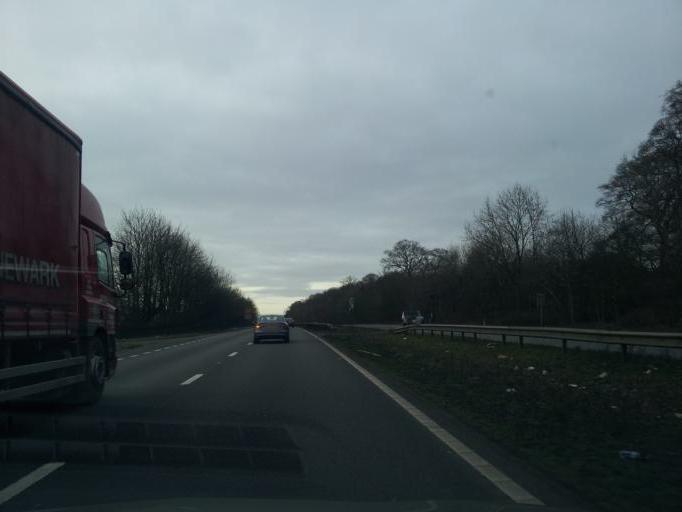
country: GB
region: England
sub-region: Lincolnshire
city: Grantham
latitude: 52.8476
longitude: -0.6275
